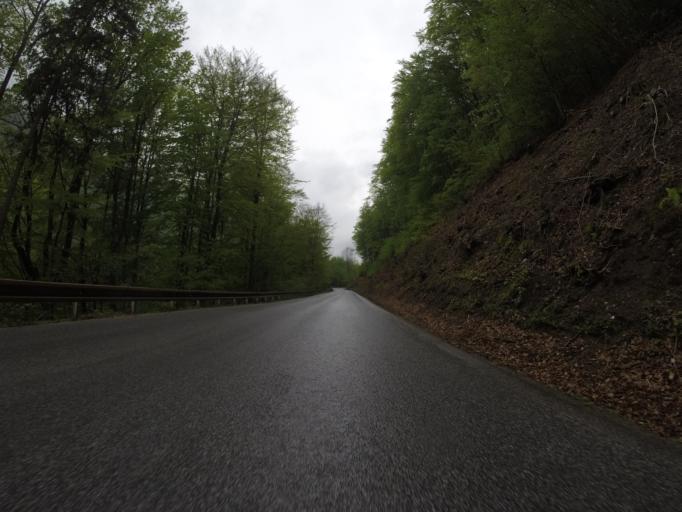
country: SK
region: Banskobystricky
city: Revuca
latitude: 48.7595
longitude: 20.0775
